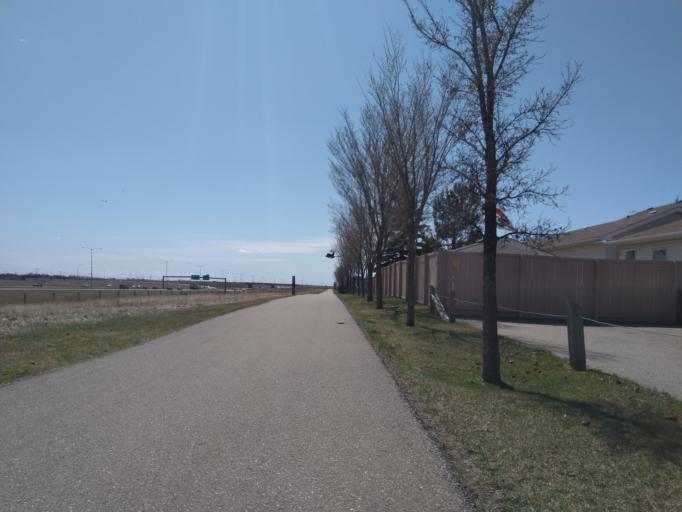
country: CA
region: Alberta
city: Chestermere
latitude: 51.0467
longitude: -113.9230
